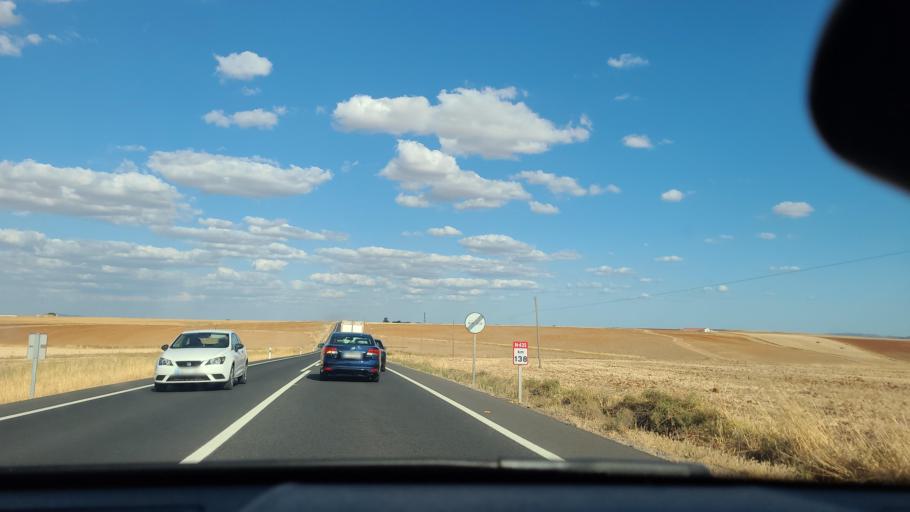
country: ES
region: Extremadura
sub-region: Provincia de Badajoz
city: Azuaga
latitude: 38.2650
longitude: -5.7507
